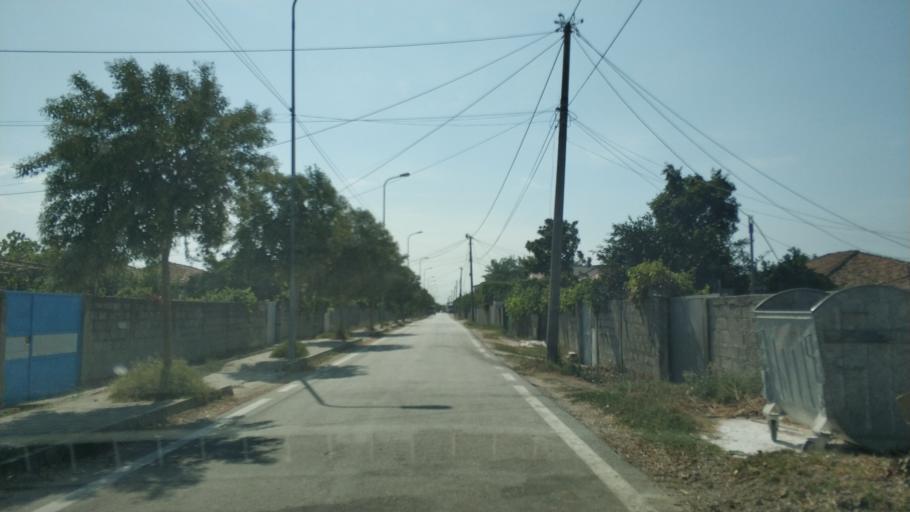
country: AL
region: Fier
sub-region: Rrethi i Fierit
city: Dermenas
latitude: 40.7331
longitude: 19.4715
